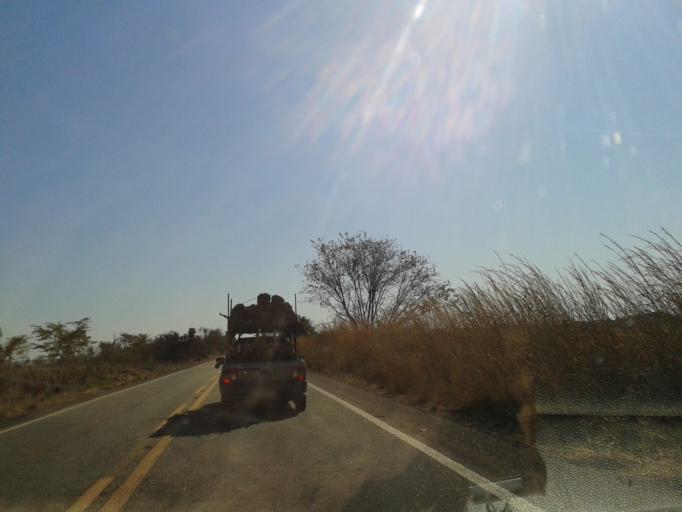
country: BR
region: Goias
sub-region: Mozarlandia
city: Mozarlandia
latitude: -14.5519
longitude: -50.4939
